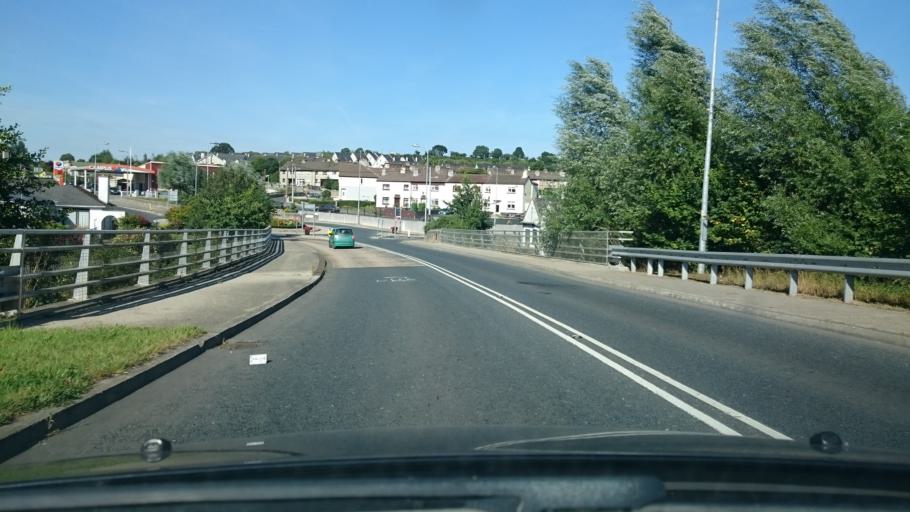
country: IE
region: Leinster
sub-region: Kilkenny
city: Graiguenamanagh
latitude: 52.5434
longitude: -6.9599
